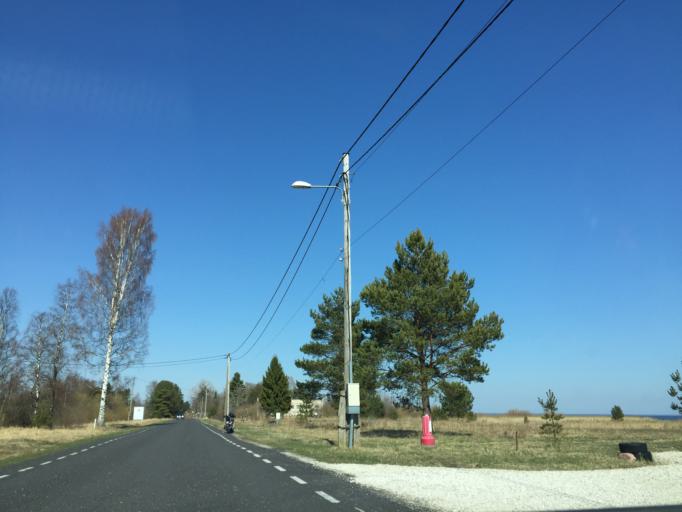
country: EE
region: Jogevamaa
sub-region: Mustvee linn
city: Mustvee
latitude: 58.8630
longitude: 26.9520
